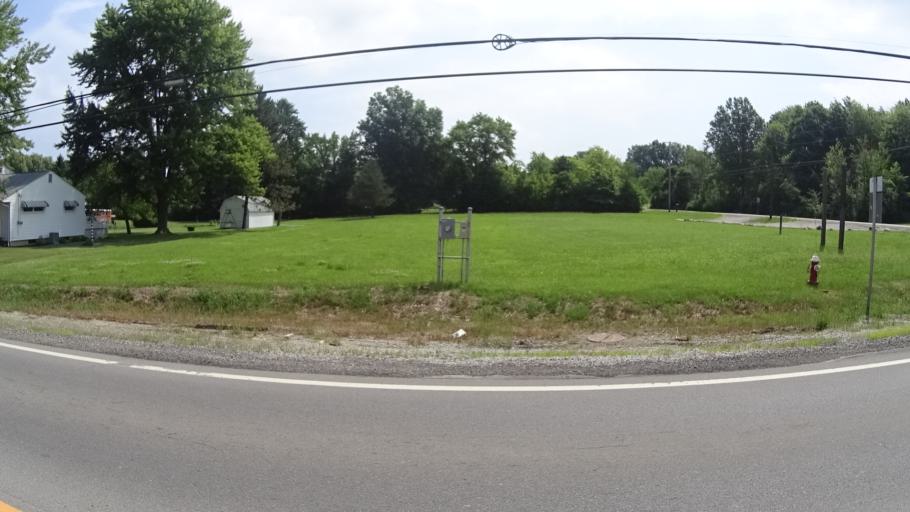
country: US
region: Ohio
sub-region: Lorain County
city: Vermilion
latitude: 41.3886
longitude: -82.3645
